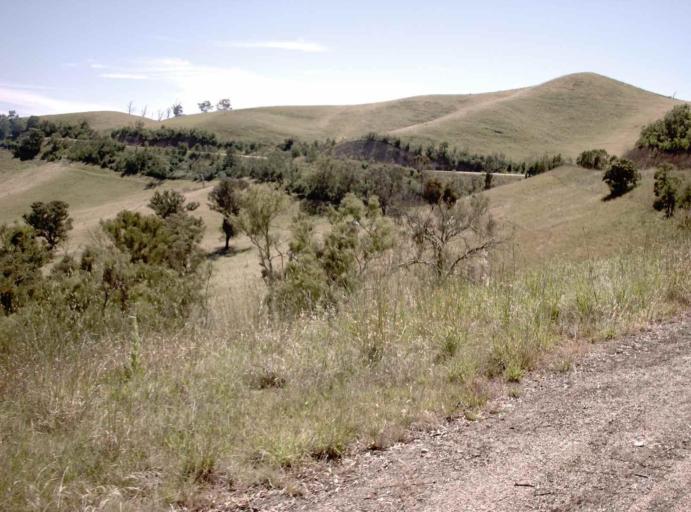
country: AU
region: Victoria
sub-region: East Gippsland
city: Lakes Entrance
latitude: -37.4924
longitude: 148.1819
